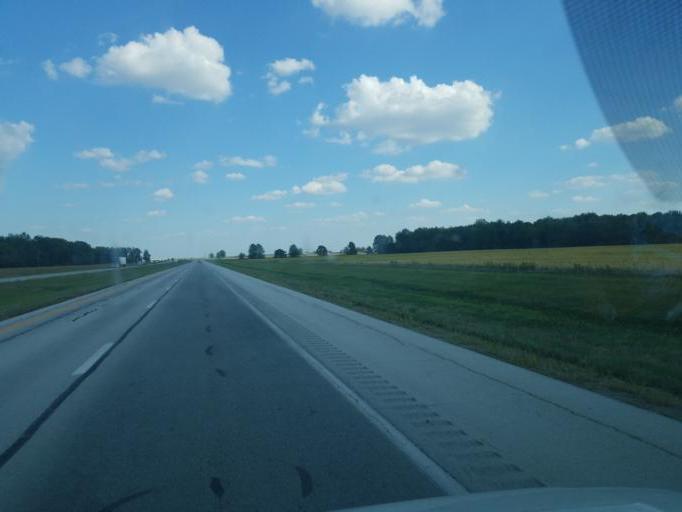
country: US
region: Ohio
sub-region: Hardin County
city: Forest
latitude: 40.8240
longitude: -83.4438
